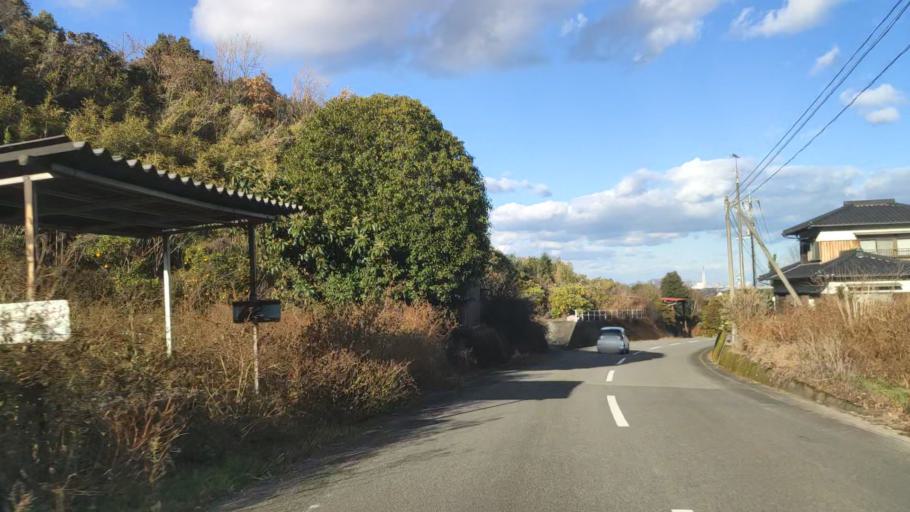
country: JP
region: Ehime
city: Saijo
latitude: 33.8881
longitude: 133.1293
